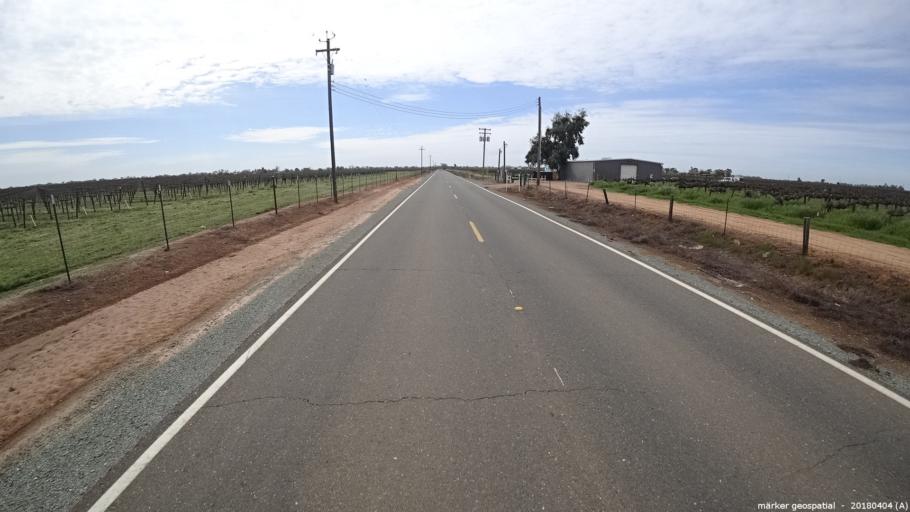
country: US
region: California
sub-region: Sacramento County
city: Clay
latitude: 38.2732
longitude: -121.1713
